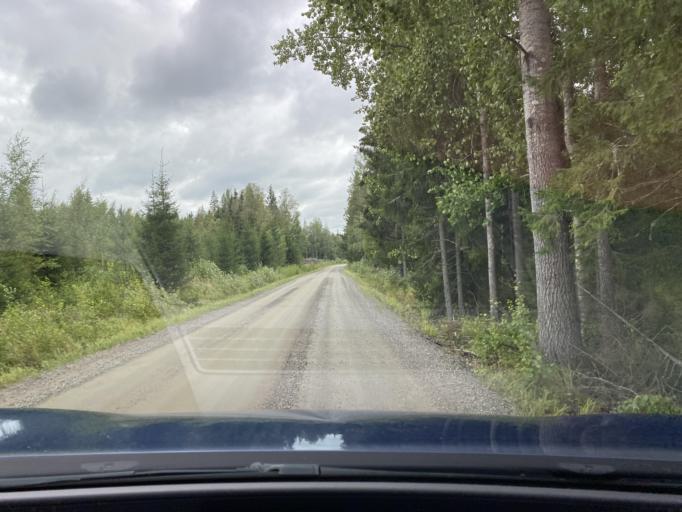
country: FI
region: Pirkanmaa
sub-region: Lounais-Pirkanmaa
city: Punkalaidun
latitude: 61.2069
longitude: 23.1783
